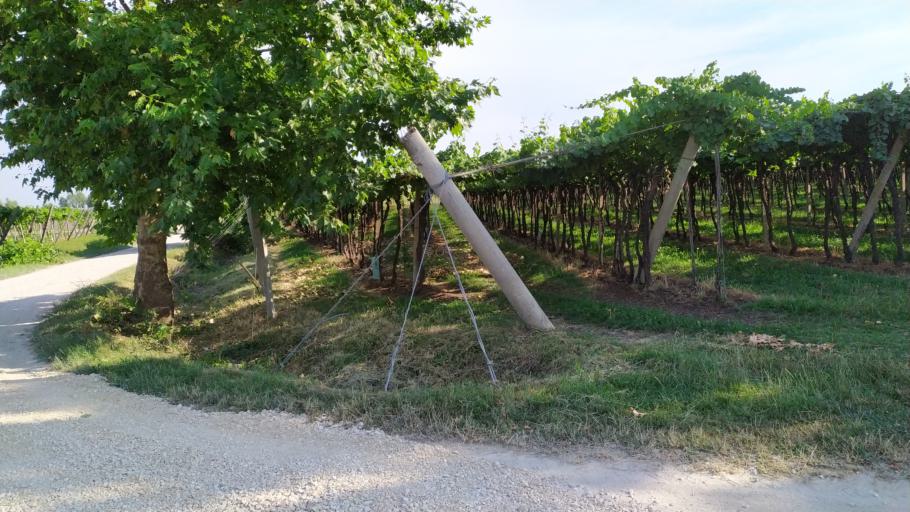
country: IT
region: Veneto
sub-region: Provincia di Verona
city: Monteforte d'Alpone
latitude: 45.4175
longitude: 11.3028
